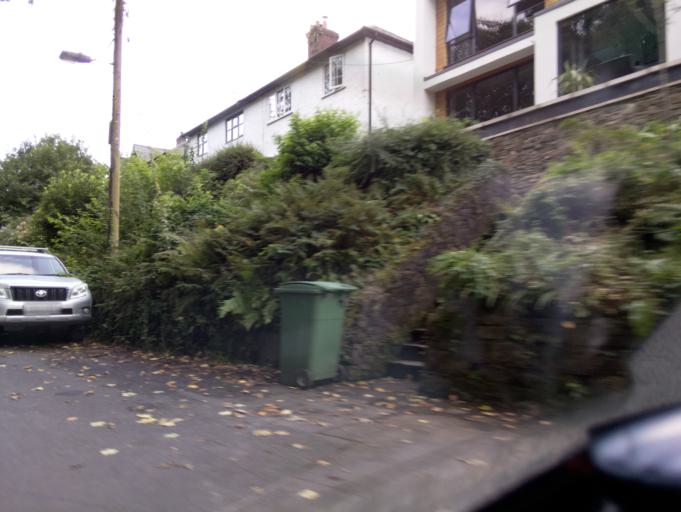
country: GB
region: Wales
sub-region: Cardiff
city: Pentyrch
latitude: 51.5460
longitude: -3.2757
